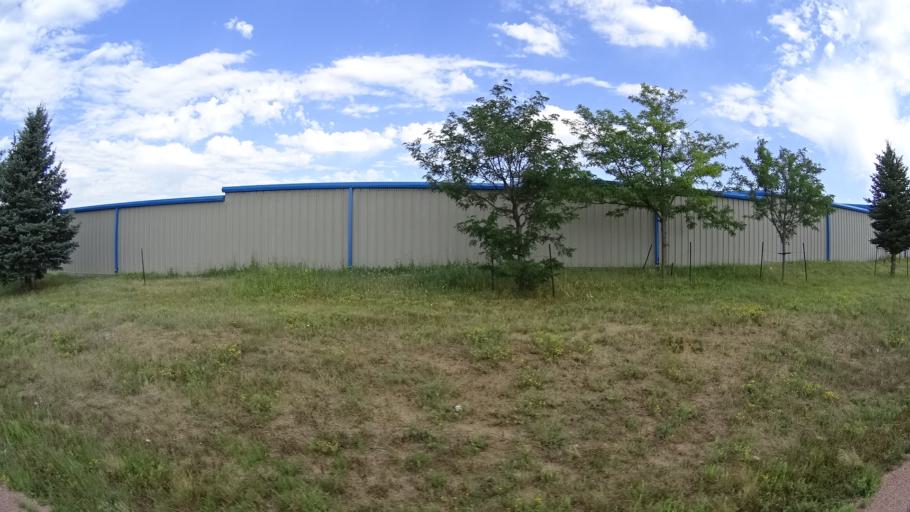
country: US
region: Colorado
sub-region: El Paso County
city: Cimarron Hills
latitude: 38.9074
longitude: -104.6791
